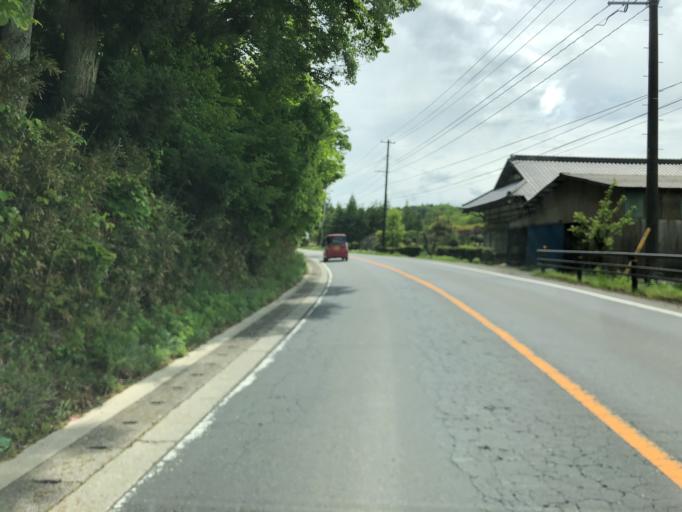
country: JP
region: Fukushima
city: Ishikawa
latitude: 37.0810
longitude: 140.3577
